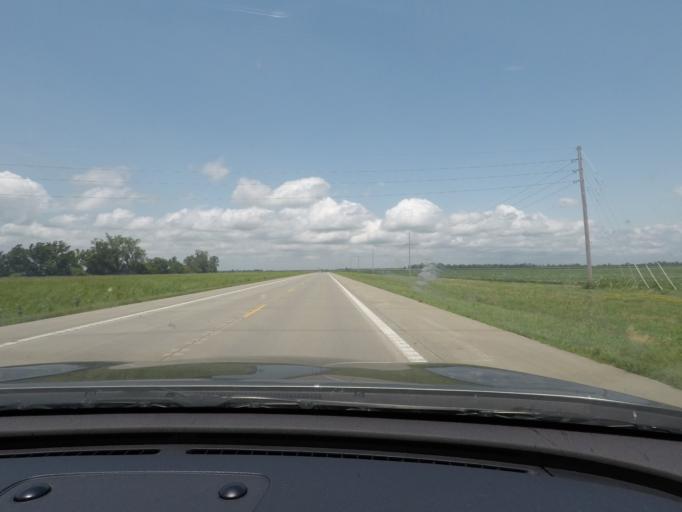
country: US
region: Missouri
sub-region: Carroll County
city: Carrollton
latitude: 39.2267
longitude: -93.5125
